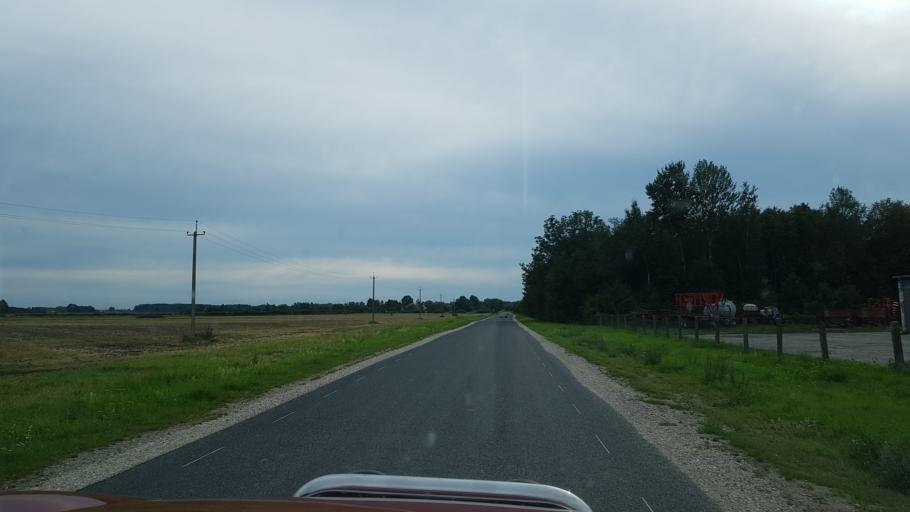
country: EE
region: Laeaene
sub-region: Lihula vald
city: Lihula
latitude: 58.8856
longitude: 23.8657
